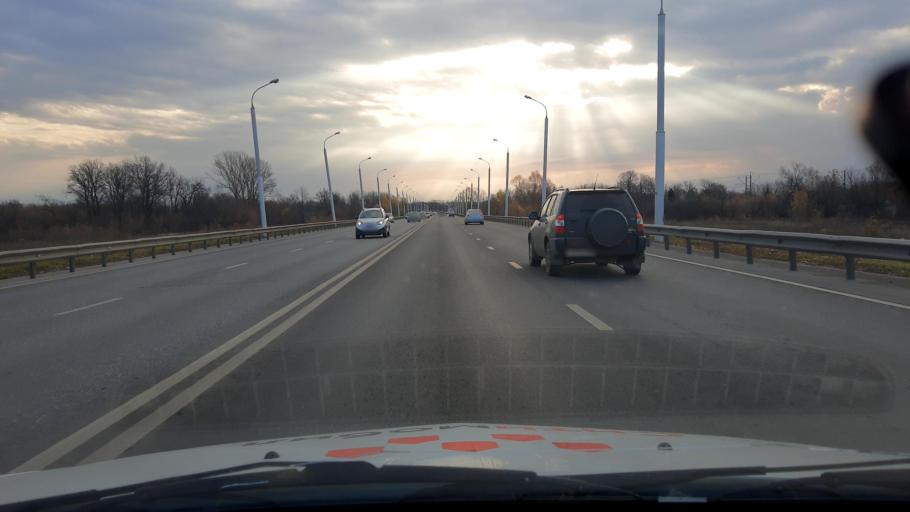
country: RU
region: Bashkortostan
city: Iglino
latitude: 54.8027
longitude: 56.1883
